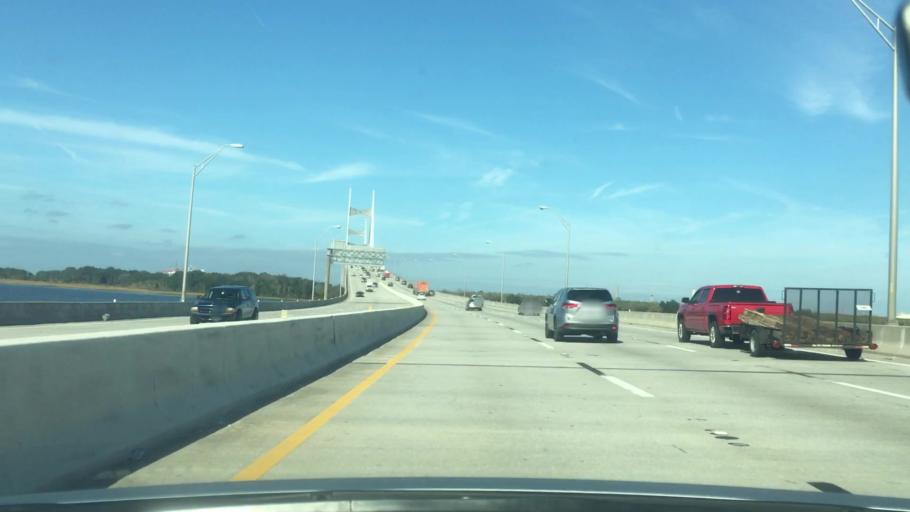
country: US
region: Florida
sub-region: Duval County
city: Jacksonville
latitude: 30.3722
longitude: -81.5527
